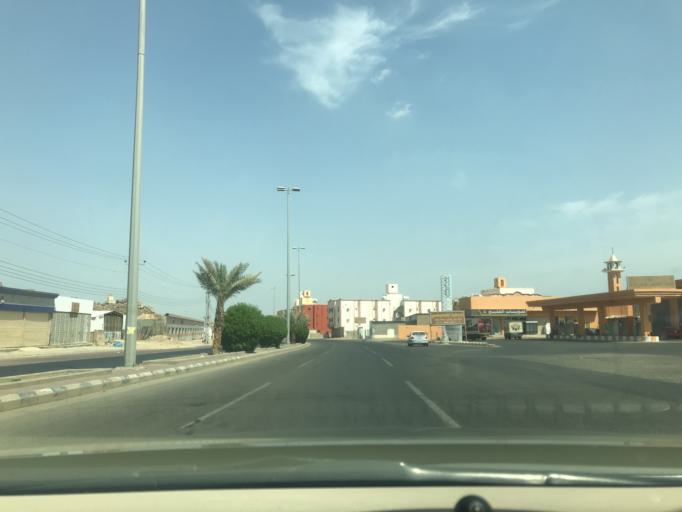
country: SA
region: Makkah
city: Al Jumum
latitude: 21.6256
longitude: 39.6688
